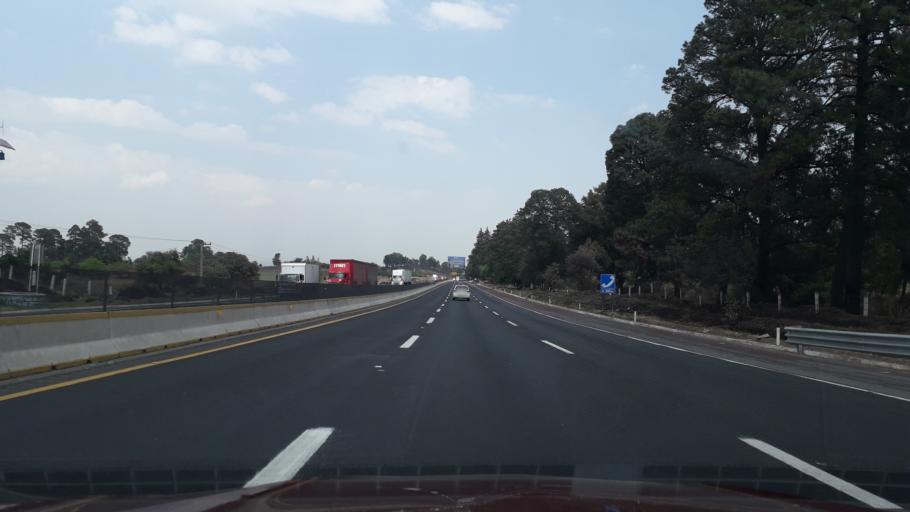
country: MX
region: Puebla
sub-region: Tlahuapan
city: Santa Cruz Otlatla
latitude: 19.3473
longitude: -98.6120
